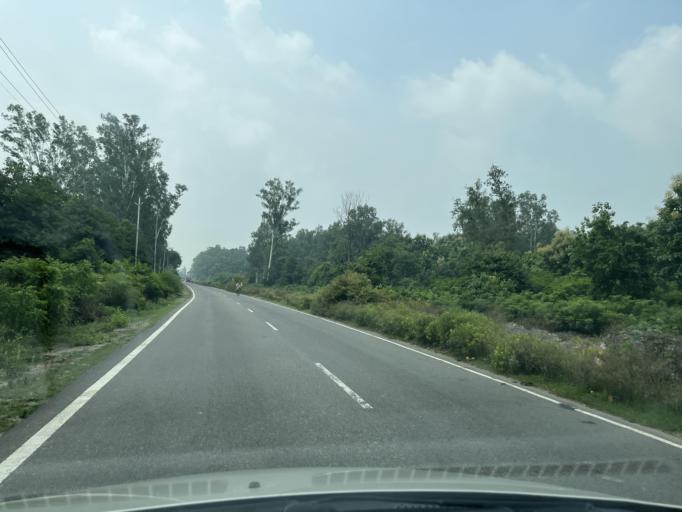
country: IN
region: Uttarakhand
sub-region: Haridwar
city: Sultanpur
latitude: 29.7590
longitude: 78.2685
